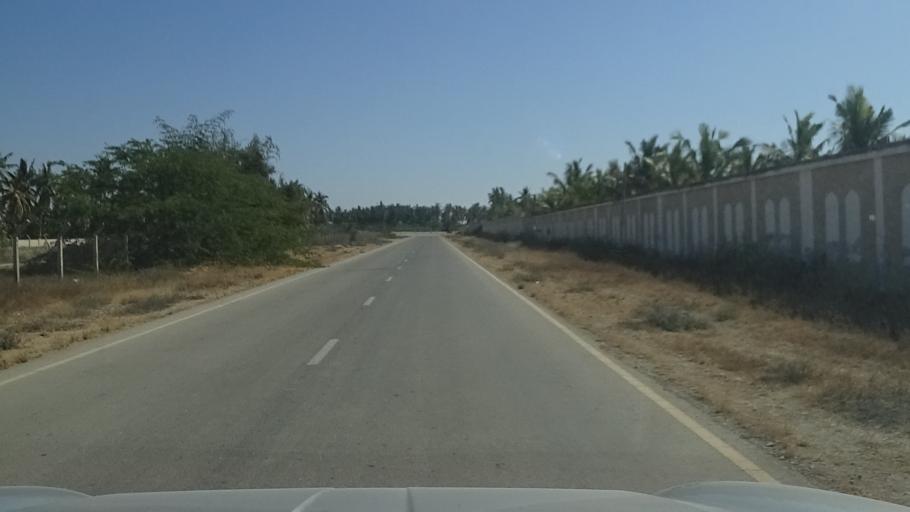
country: OM
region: Zufar
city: Salalah
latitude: 17.0335
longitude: 54.1511
